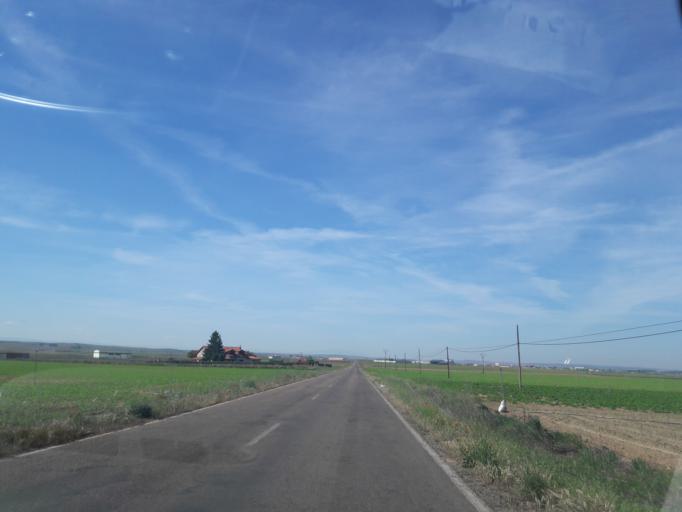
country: ES
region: Castille and Leon
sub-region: Provincia de Salamanca
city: Villoruela
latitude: 41.0031
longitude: -5.3985
